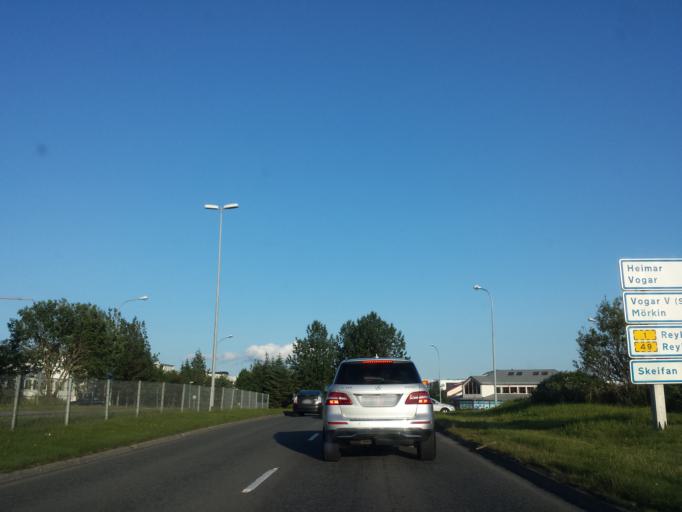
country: IS
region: Capital Region
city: Reykjavik
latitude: 64.1307
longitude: -21.8642
